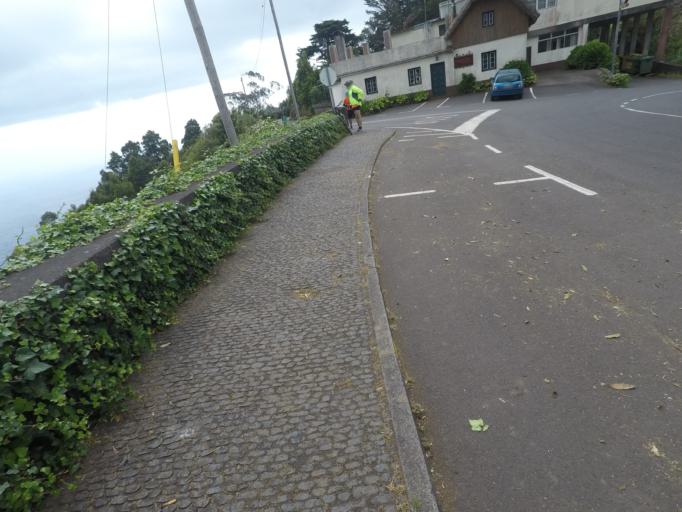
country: PT
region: Madeira
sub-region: Santa Cruz
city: Santa Cruz
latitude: 32.7472
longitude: -16.8259
